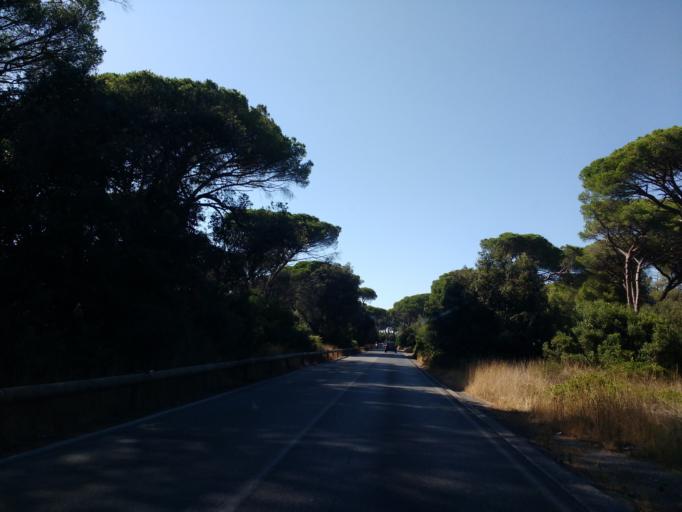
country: IT
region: Latium
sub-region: Citta metropolitana di Roma Capitale
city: Acilia-Castel Fusano-Ostia Antica
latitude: 41.7217
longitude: 12.3465
